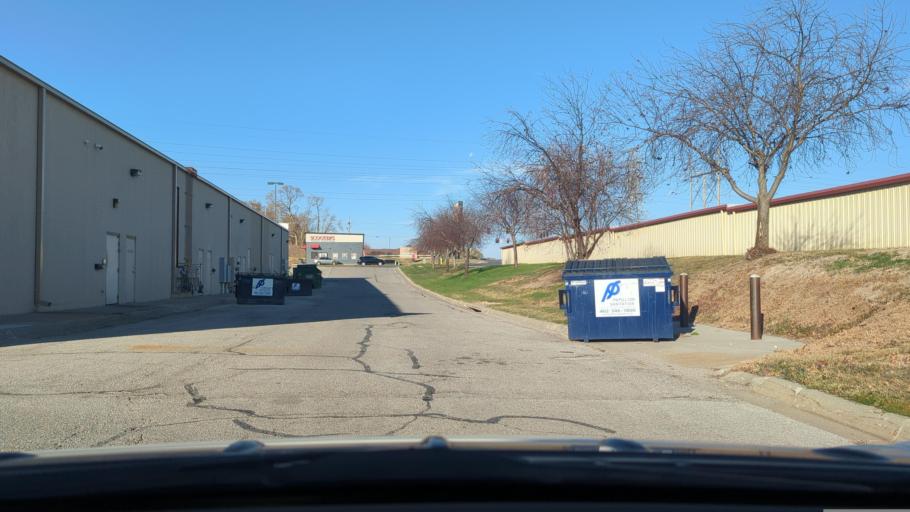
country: US
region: Nebraska
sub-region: Sarpy County
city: Offutt Air Force Base
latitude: 41.1564
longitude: -95.9317
